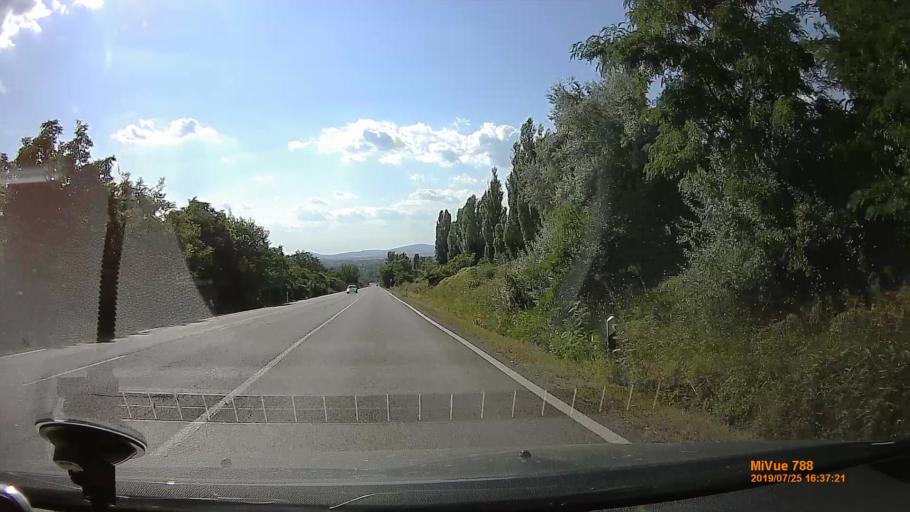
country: HU
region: Heves
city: Gyongyos
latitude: 47.7719
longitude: 19.9628
